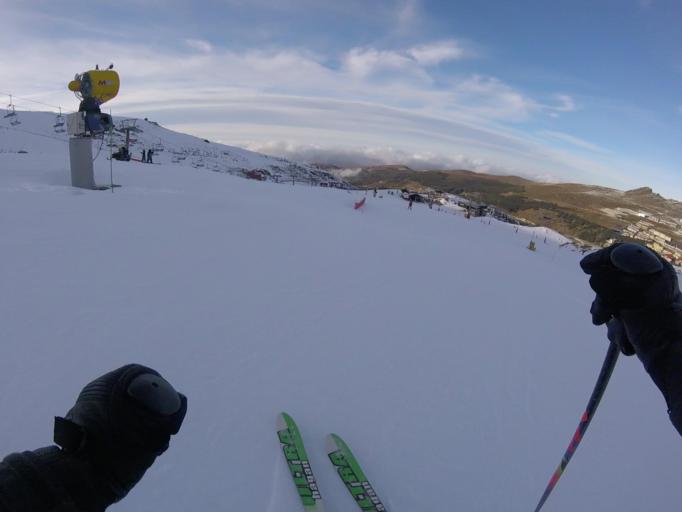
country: ES
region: Andalusia
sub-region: Provincia de Granada
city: Guejar-Sierra
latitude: 37.0813
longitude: -3.4050
